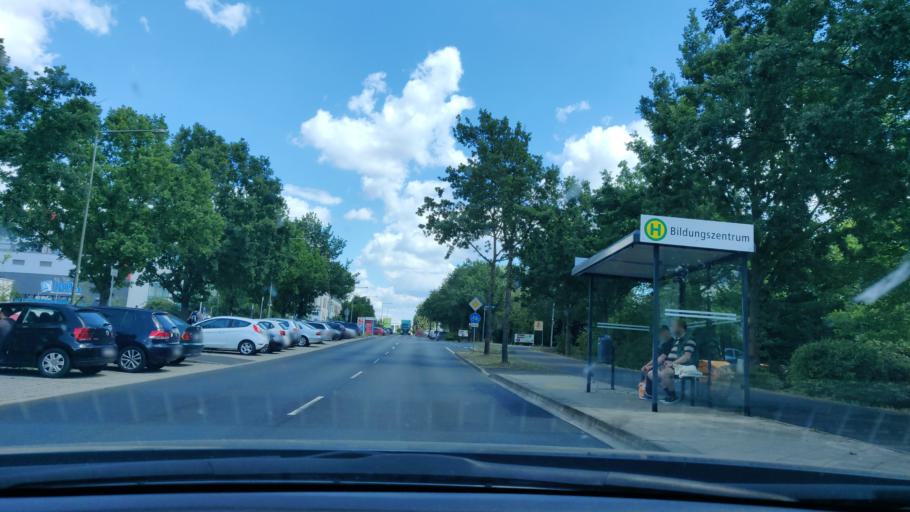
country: DE
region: Hesse
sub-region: Regierungsbezirk Kassel
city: Fuldabruck
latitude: 51.2830
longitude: 9.4982
